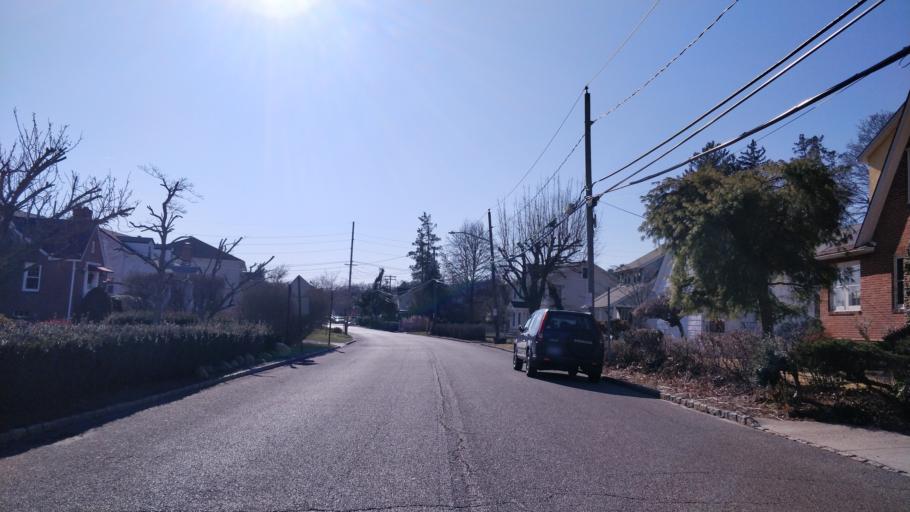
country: US
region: New York
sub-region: Nassau County
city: Glen Head
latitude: 40.8365
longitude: -73.6238
